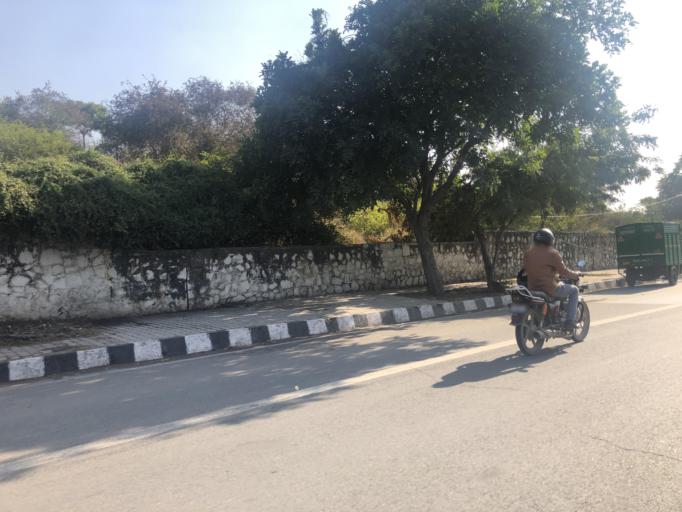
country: IN
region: NCT
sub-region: Central Delhi
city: Karol Bagh
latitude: 28.5497
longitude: 77.1637
